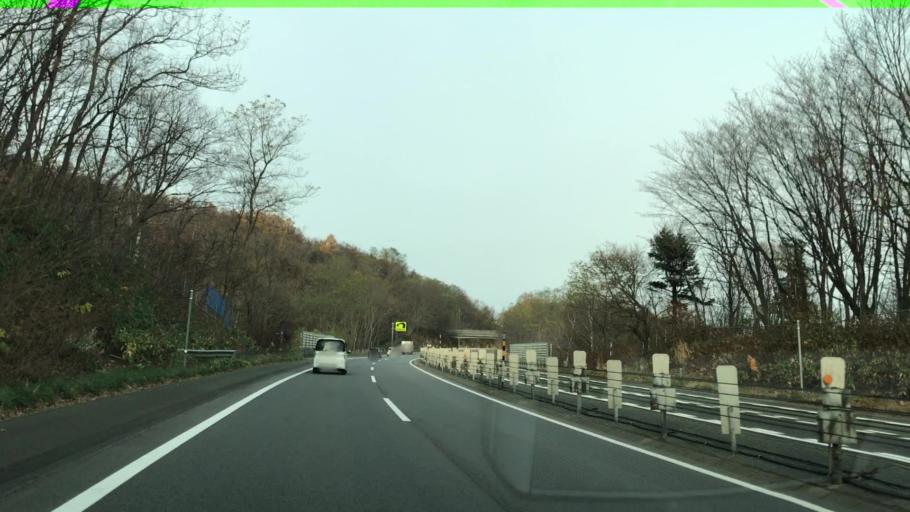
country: JP
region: Hokkaido
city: Otaru
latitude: 43.1467
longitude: 141.1337
